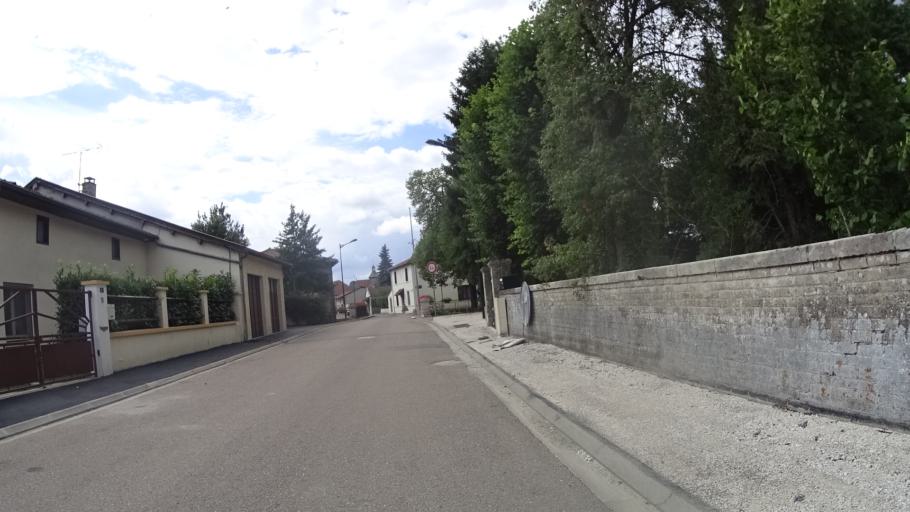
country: FR
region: Champagne-Ardenne
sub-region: Departement de la Haute-Marne
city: Villiers-en-Lieu
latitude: 48.6561
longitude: 4.8268
